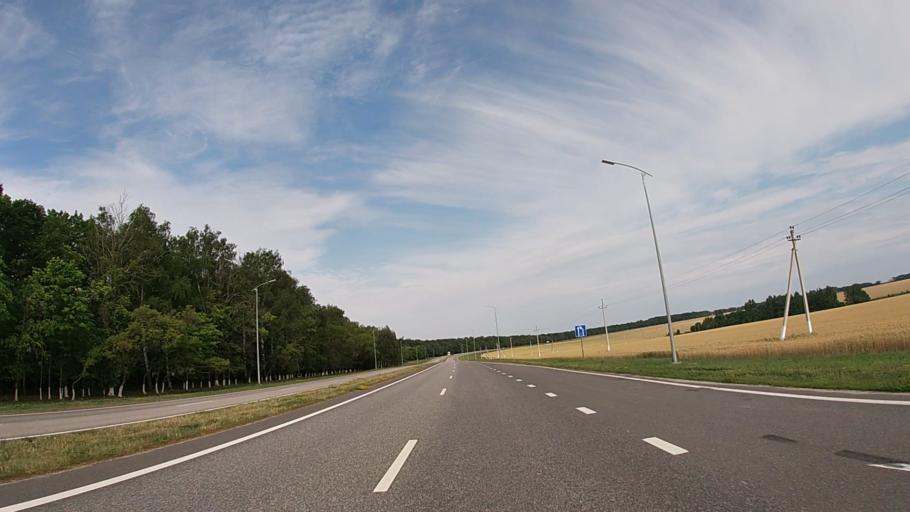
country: RU
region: Belgorod
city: Borisovka
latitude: 50.7510
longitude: 35.9797
